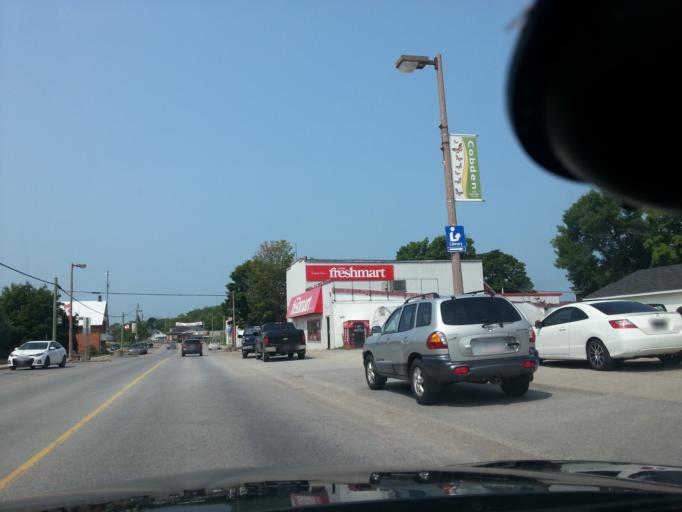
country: CA
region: Ontario
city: Renfrew
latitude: 45.6266
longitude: -76.8844
